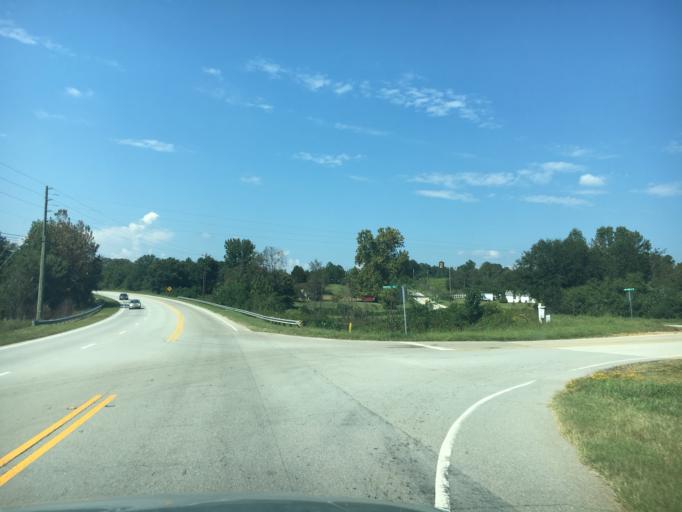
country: US
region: Georgia
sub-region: Franklin County
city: Lavonia
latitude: 34.4492
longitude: -83.0363
